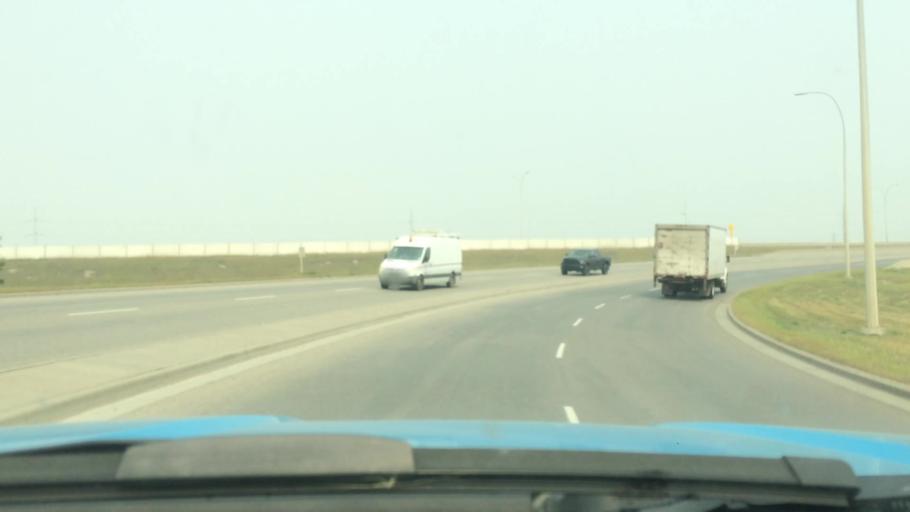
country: CA
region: Alberta
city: Calgary
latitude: 51.0075
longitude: -114.0144
